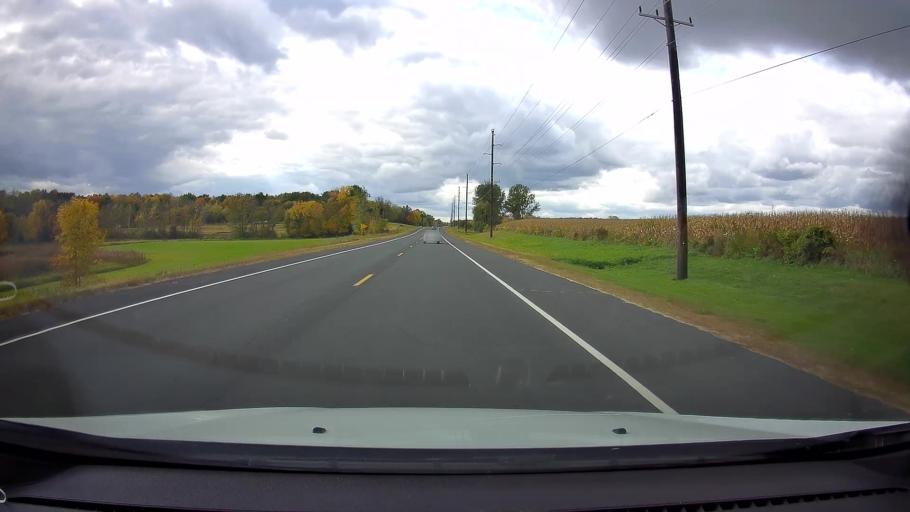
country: US
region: Minnesota
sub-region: Chisago County
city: Center City
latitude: 45.3971
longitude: -92.7879
